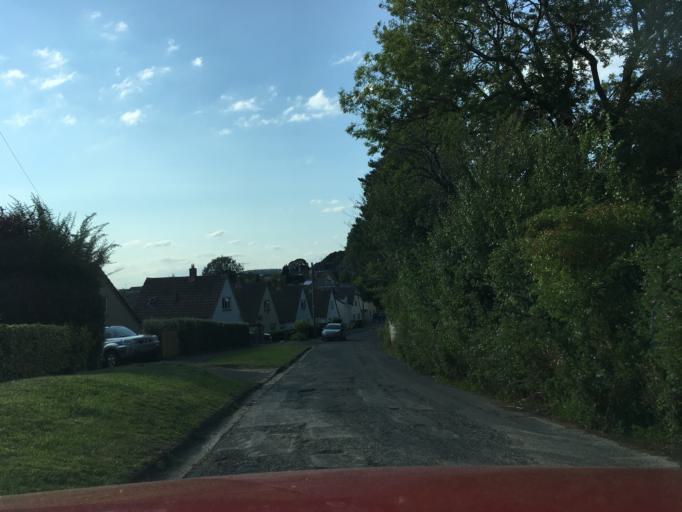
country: GB
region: England
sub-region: Gloucestershire
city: Stroud
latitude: 51.7357
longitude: -2.2270
